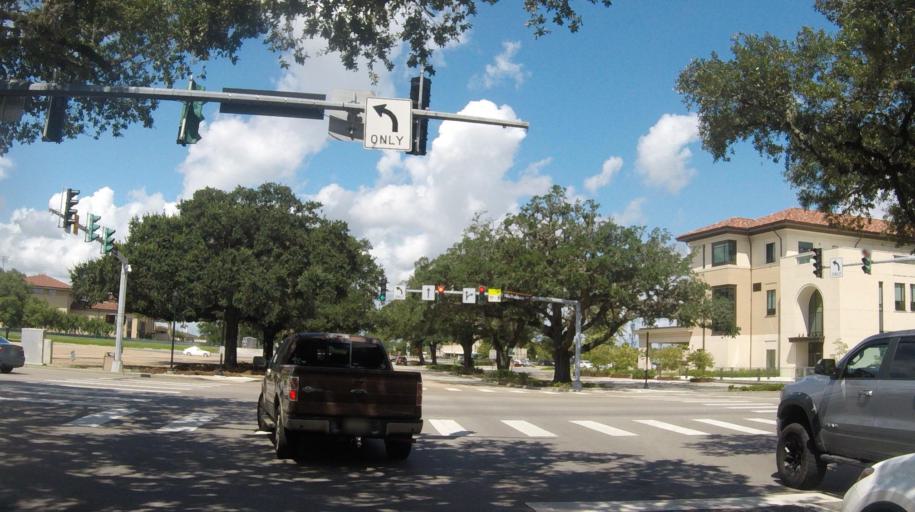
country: US
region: Louisiana
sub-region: West Baton Rouge Parish
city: Port Allen
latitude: 30.4111
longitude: -91.1861
